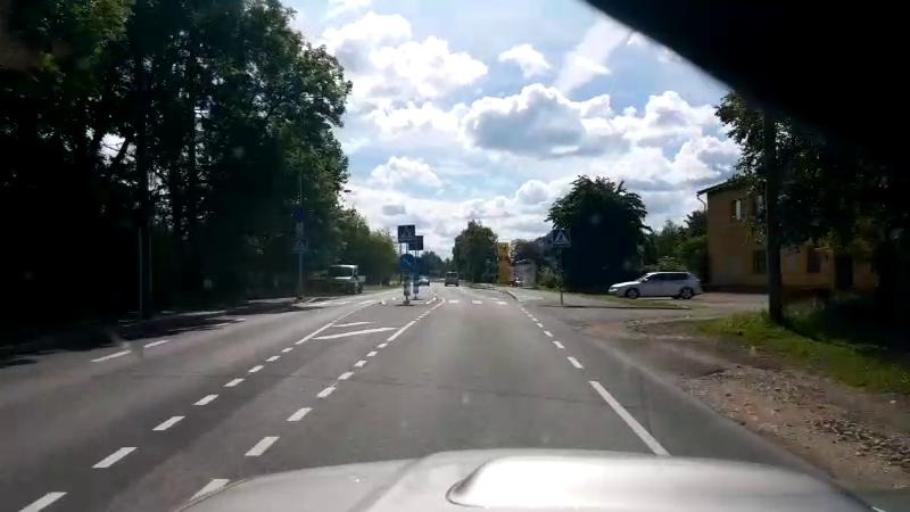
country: EE
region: Laeaene-Virumaa
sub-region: Tapa vald
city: Tapa
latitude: 59.2544
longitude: 25.9741
